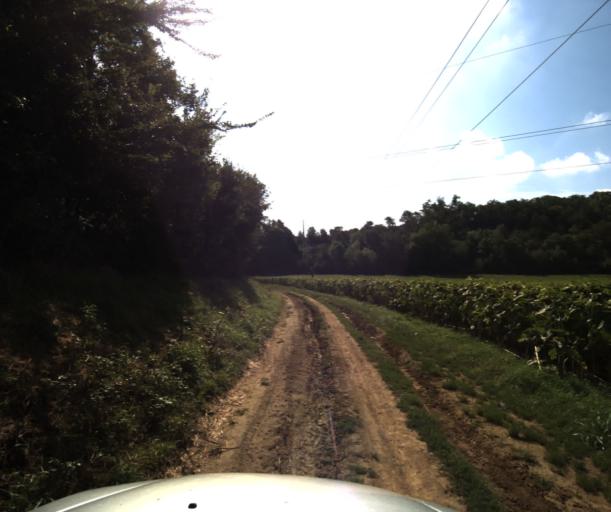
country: FR
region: Midi-Pyrenees
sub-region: Departement de la Haute-Garonne
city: Portet-sur-Garonne
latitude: 43.5178
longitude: 1.4231
